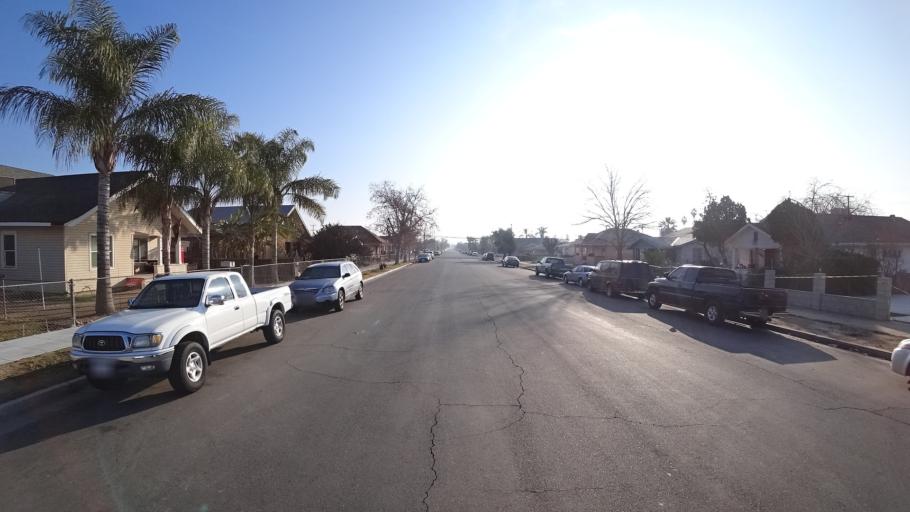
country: US
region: California
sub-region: Kern County
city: Bakersfield
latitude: 35.3819
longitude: -118.9855
